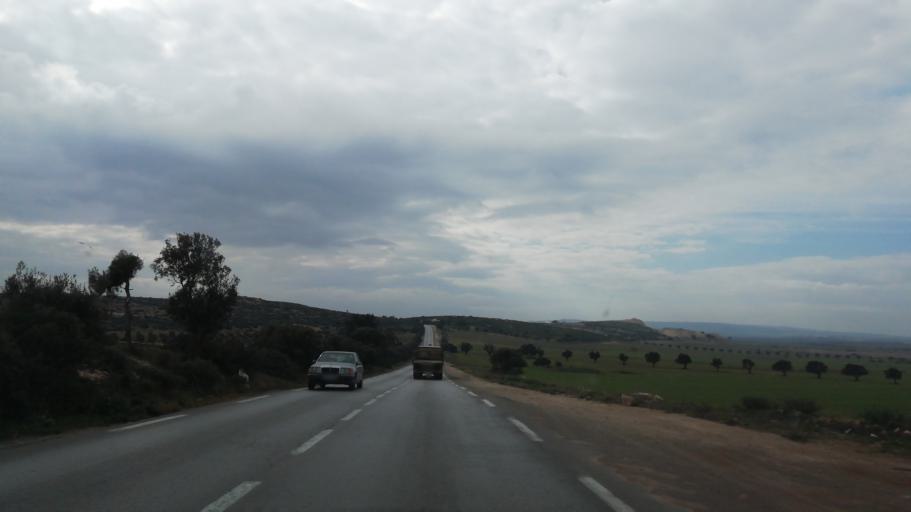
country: DZ
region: Oran
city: Ain el Bya
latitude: 35.7261
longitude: -0.3555
